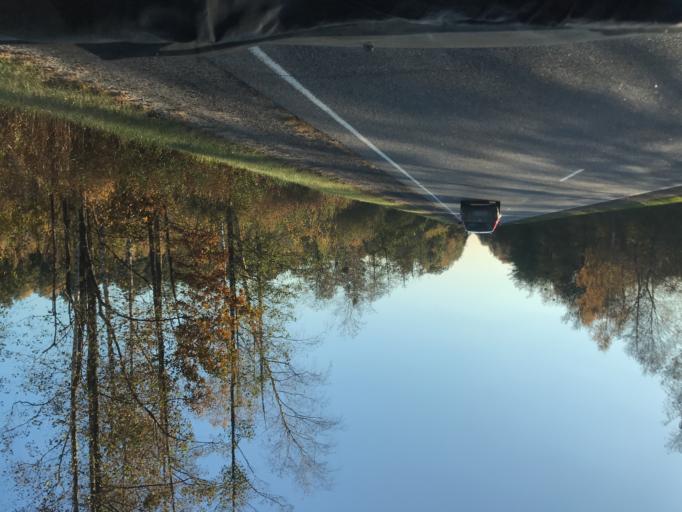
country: BY
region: Gomel
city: Zhytkavichy
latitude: 52.2742
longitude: 28.1507
